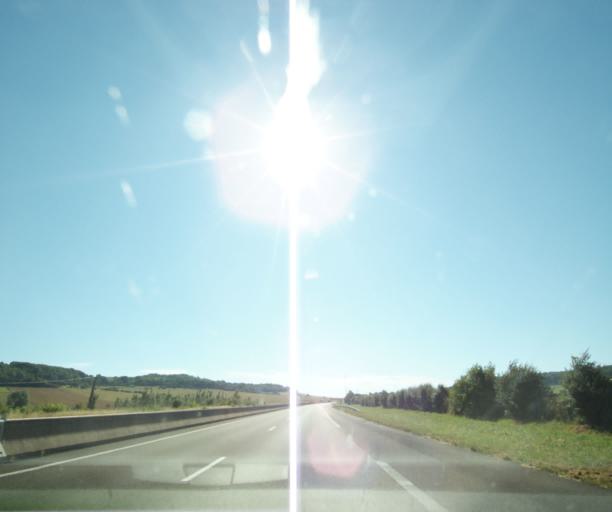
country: FR
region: Champagne-Ardenne
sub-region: Departement de la Haute-Marne
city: Nogent-le-Bas
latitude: 47.9573
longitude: 5.4059
